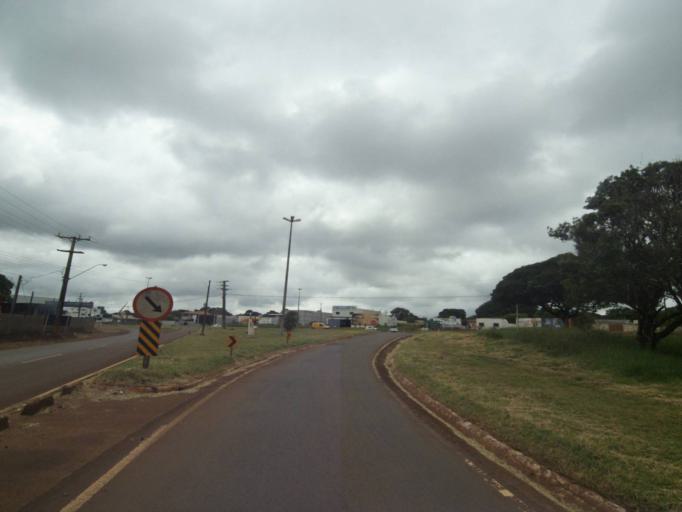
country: BR
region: Parana
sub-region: Campo Mourao
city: Campo Mourao
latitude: -24.0205
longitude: -52.3646
